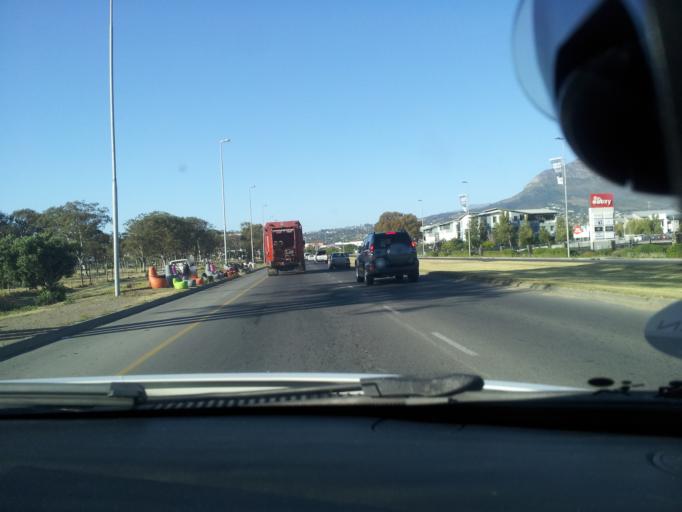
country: ZA
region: Western Cape
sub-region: Cape Winelands District Municipality
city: Stellenbosch
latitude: -34.0887
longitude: 18.8193
